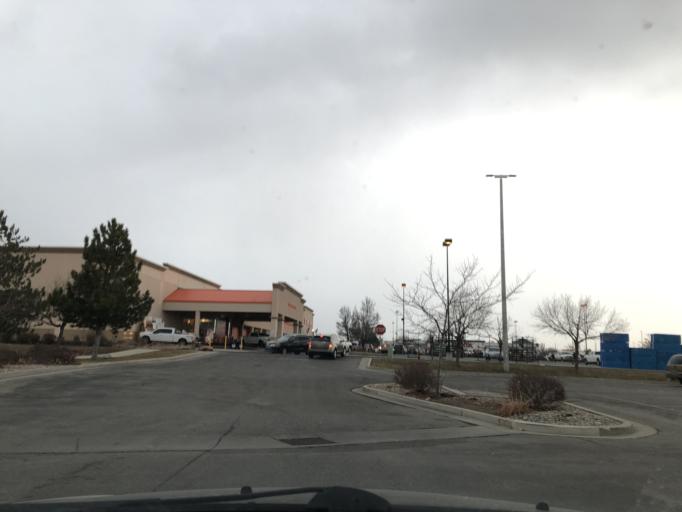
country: US
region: Utah
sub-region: Cache County
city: Logan
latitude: 41.7547
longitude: -111.8318
